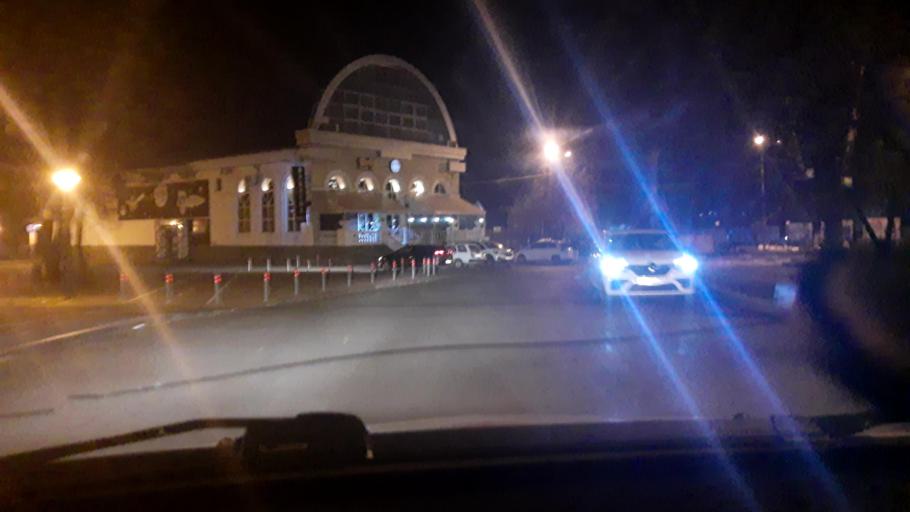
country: RU
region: Bashkortostan
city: Ufa
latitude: 54.7727
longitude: 56.0228
